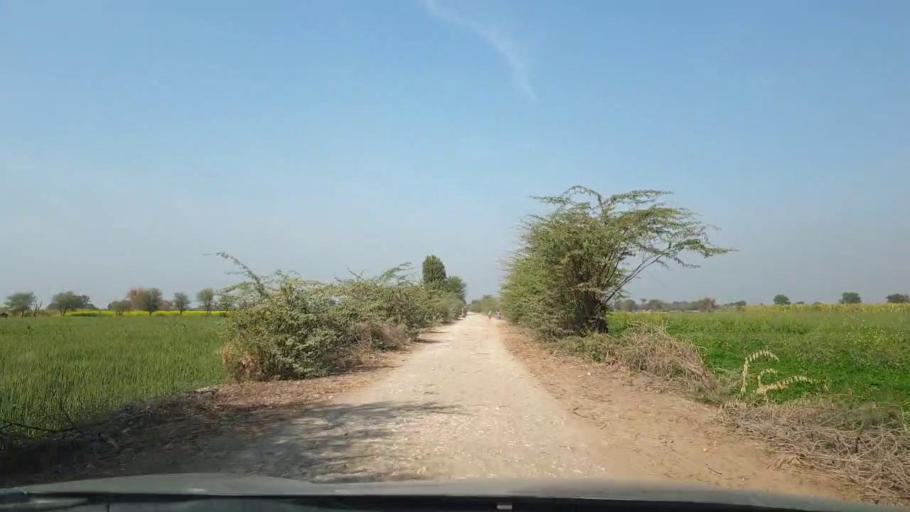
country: PK
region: Sindh
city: Berani
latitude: 25.7024
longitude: 68.7535
